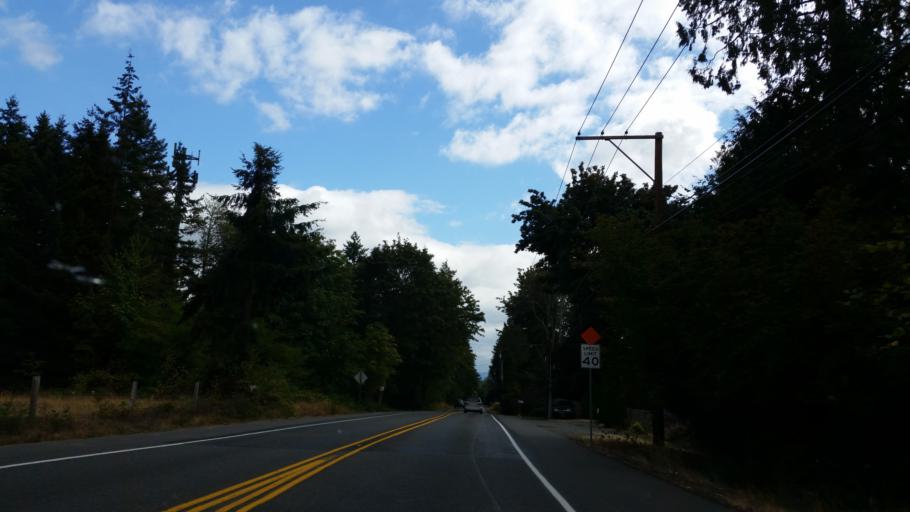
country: US
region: Washington
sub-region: Pierce County
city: Bonney Lake
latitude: 47.2204
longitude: -122.1406
